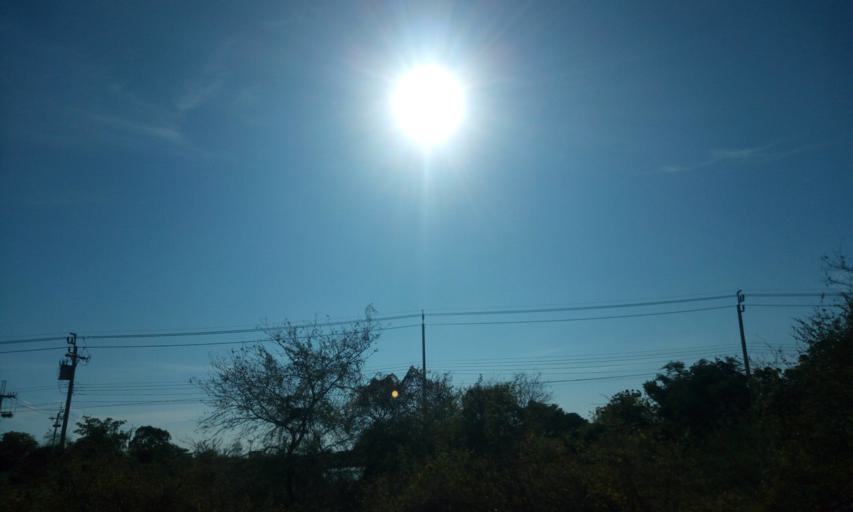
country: TH
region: Samut Prakan
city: Bang Bo District
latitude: 13.5301
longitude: 100.7486
